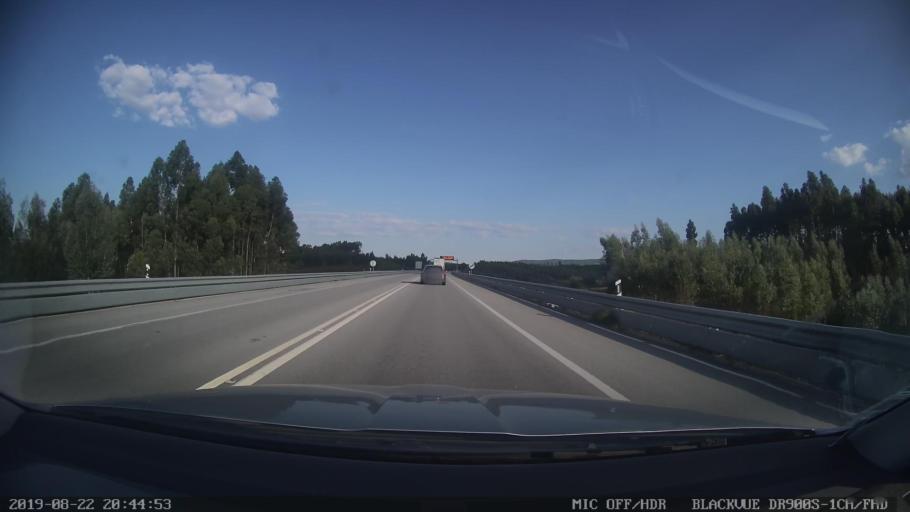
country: PT
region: Castelo Branco
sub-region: Proenca-A-Nova
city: Proenca-a-Nova
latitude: 39.7114
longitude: -7.8584
